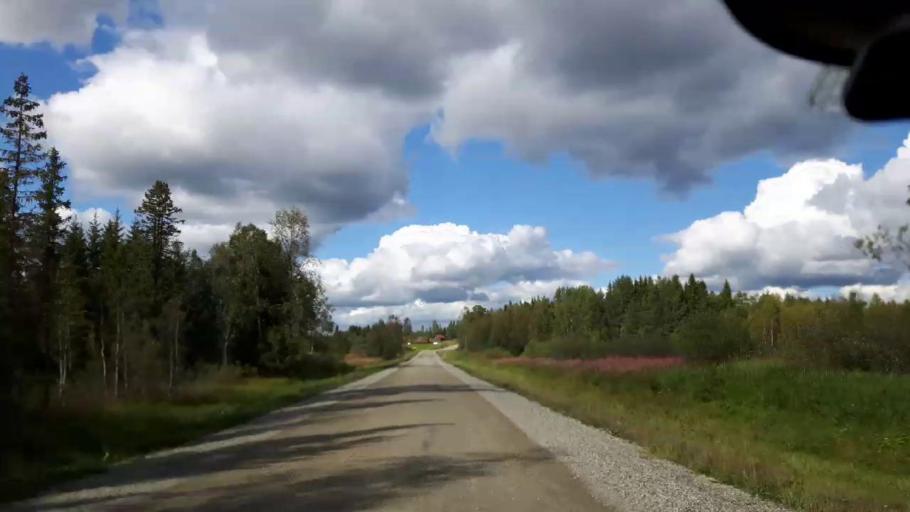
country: SE
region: Jaemtland
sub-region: Stroemsunds Kommun
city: Stroemsund
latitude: 63.3529
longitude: 15.5699
